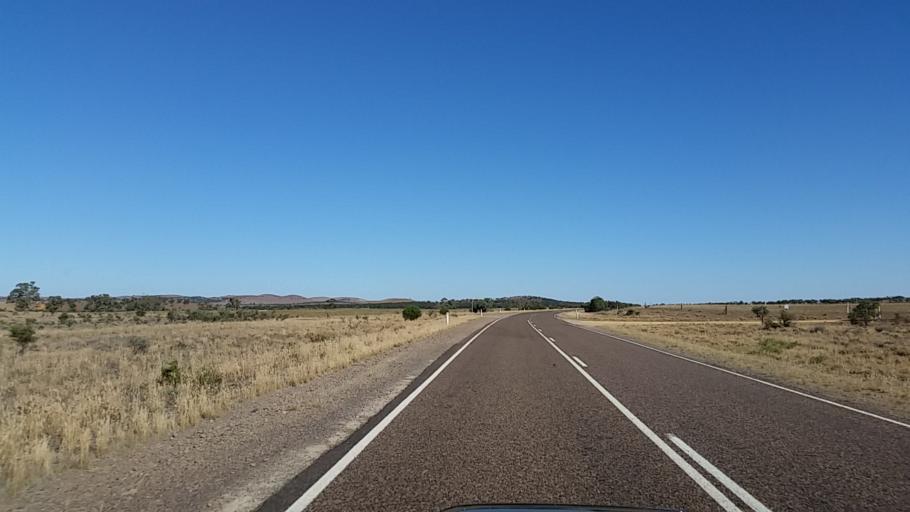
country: AU
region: South Australia
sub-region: Flinders Ranges
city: Quorn
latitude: -32.4875
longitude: 138.5455
